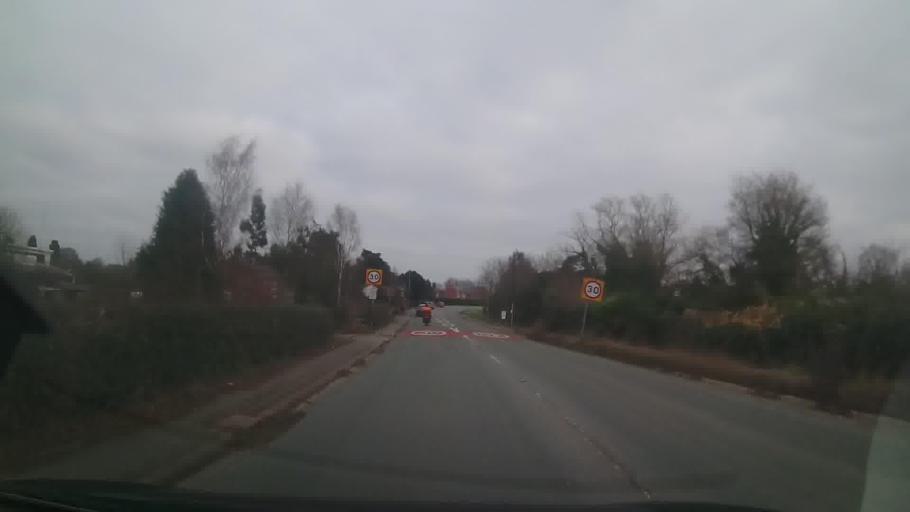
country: GB
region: England
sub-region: Shropshire
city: Bicton
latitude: 52.7264
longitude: -2.8214
